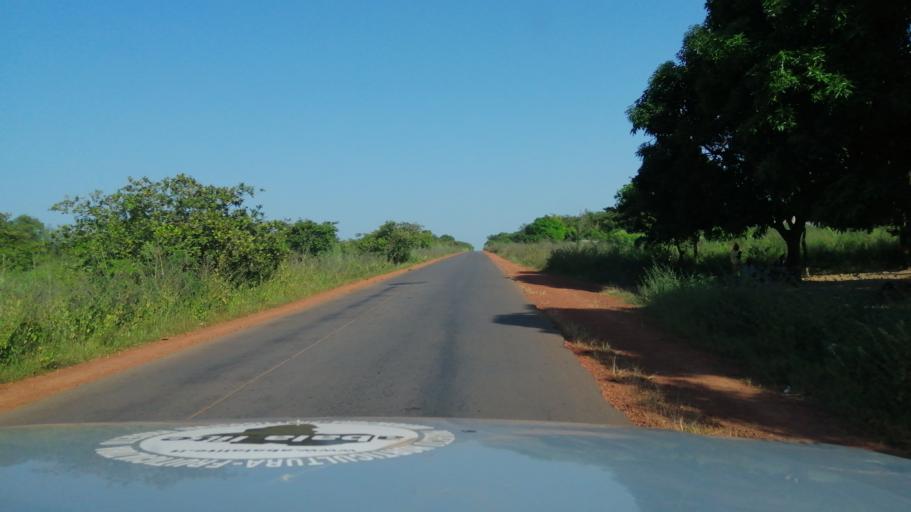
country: GW
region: Bissau
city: Bissau
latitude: 11.9588
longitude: -15.5268
